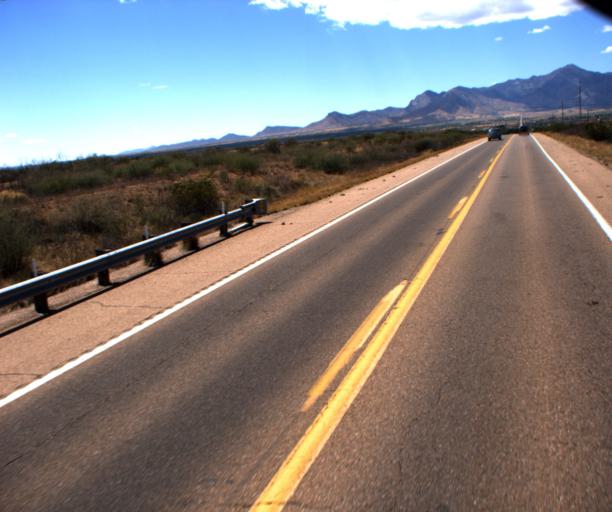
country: US
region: Arizona
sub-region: Cochise County
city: Sierra Vista Southeast
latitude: 31.3800
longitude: -110.0914
